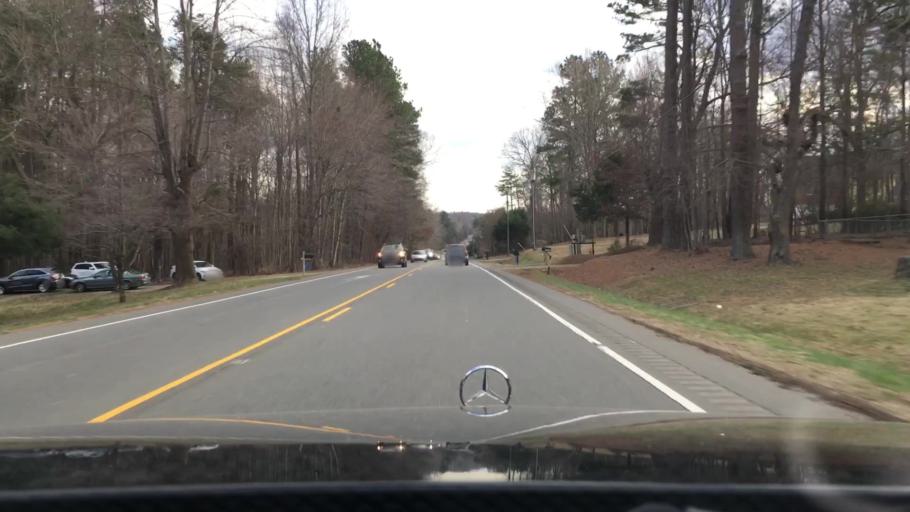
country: US
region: North Carolina
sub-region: Orange County
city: Hillsborough
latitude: 36.1289
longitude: -79.1180
